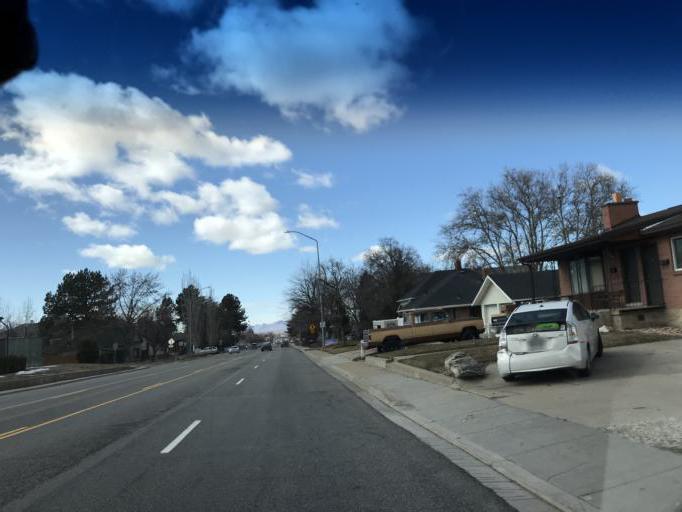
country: US
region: Utah
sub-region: Davis County
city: Bountiful
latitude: 40.8843
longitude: -111.8752
